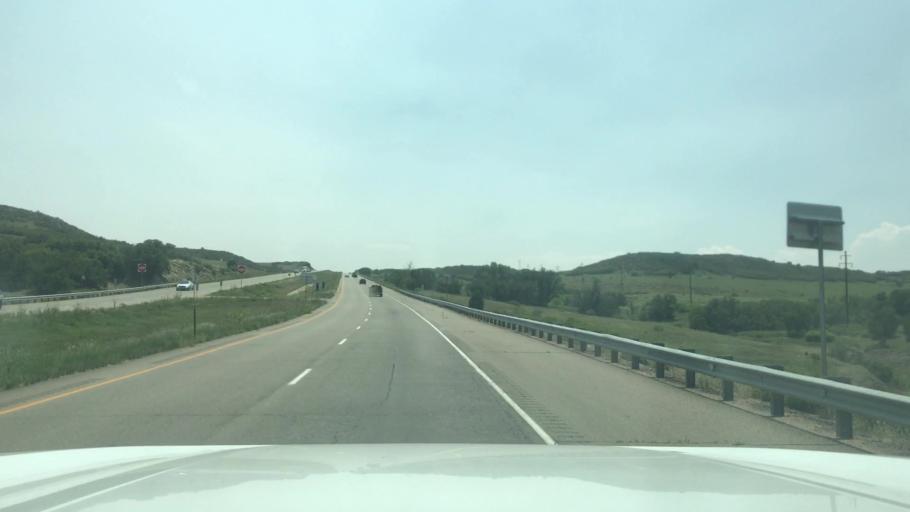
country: US
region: Colorado
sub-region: Pueblo County
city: Colorado City
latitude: 37.9088
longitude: -104.8292
